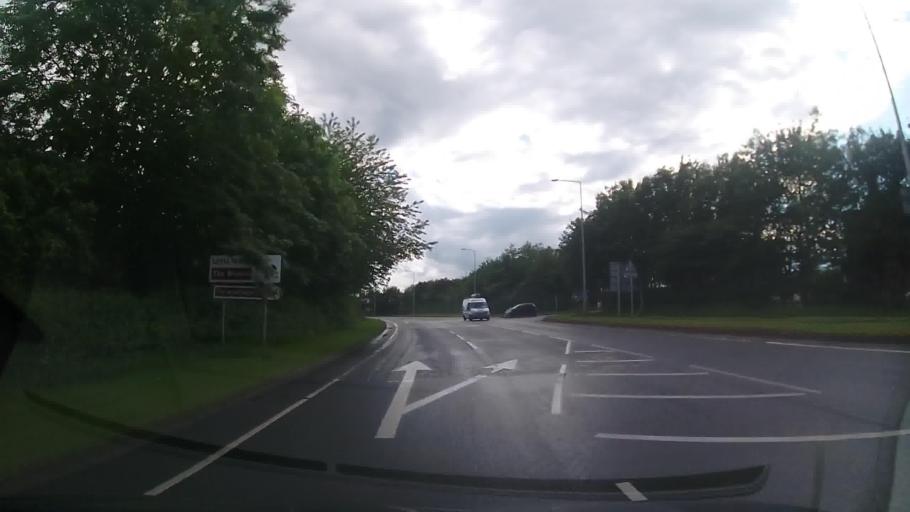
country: GB
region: England
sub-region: Telford and Wrekin
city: Ironbridge
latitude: 52.6605
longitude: -2.4897
